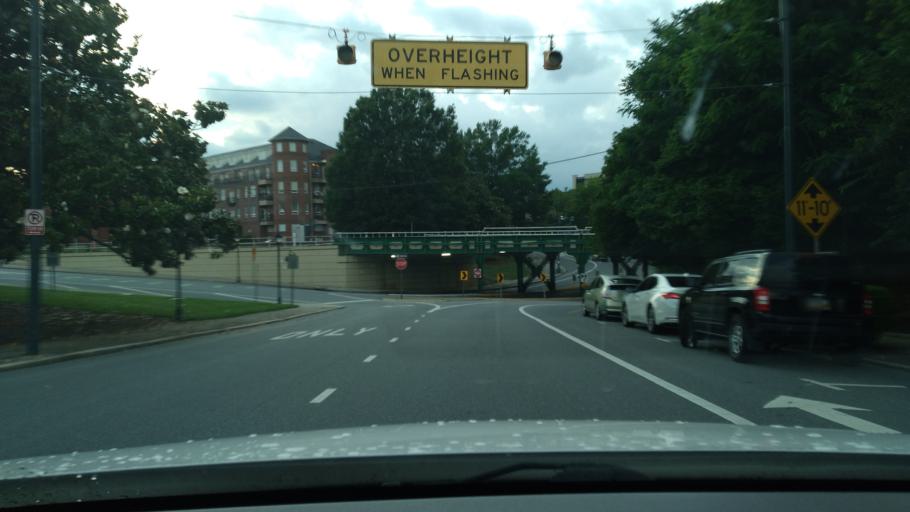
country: US
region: North Carolina
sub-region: Guilford County
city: Greensboro
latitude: 36.0673
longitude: -79.7896
